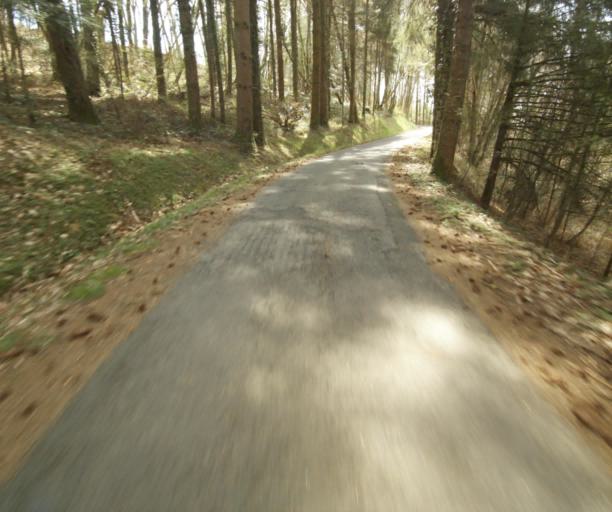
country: FR
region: Limousin
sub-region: Departement de la Correze
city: Naves
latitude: 45.3658
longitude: 1.7924
